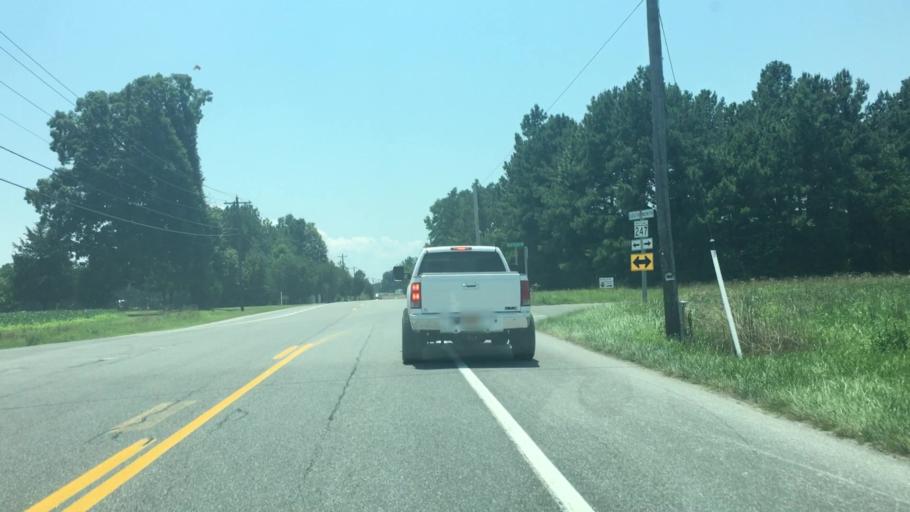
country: US
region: Maryland
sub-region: Saint Mary's County
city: Leonardtown
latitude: 38.3737
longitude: -76.6785
